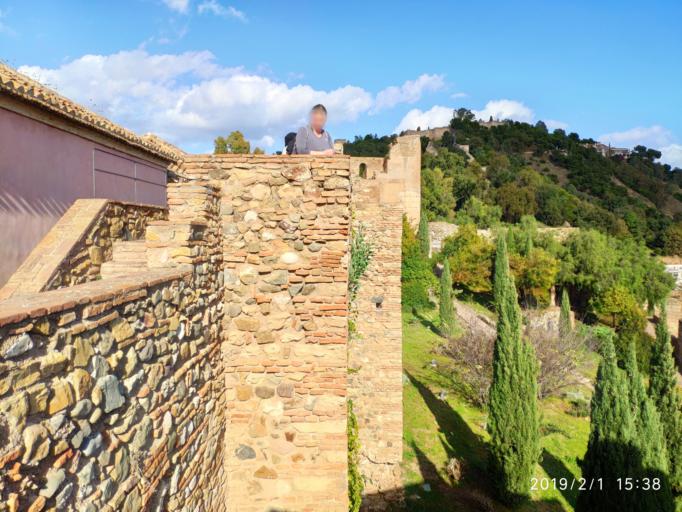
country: ES
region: Andalusia
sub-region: Provincia de Malaga
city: Malaga
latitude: 36.7210
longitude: -4.4157
